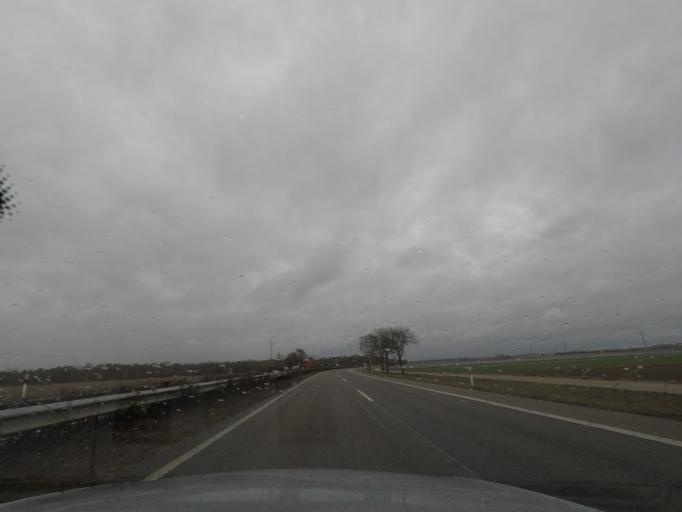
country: DE
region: Rheinland-Pfalz
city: Otterstadt
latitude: 49.3670
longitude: 8.4210
